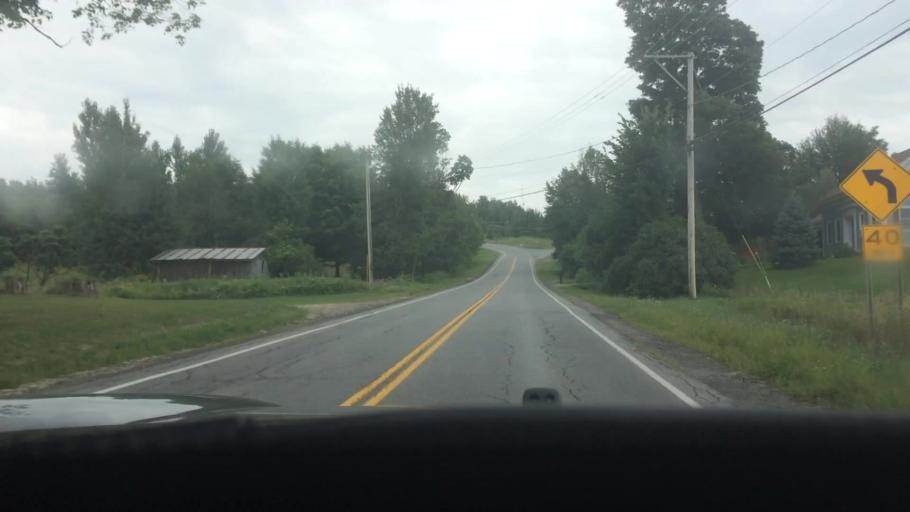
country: US
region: New York
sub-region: St. Lawrence County
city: Canton
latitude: 44.5447
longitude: -75.1016
